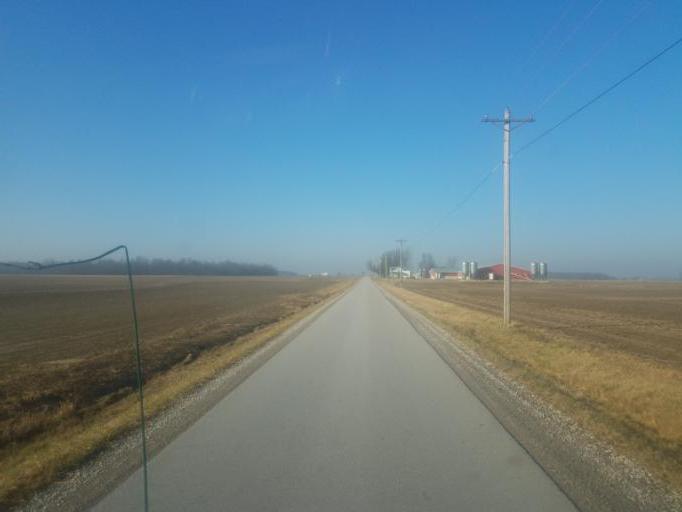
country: US
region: Ohio
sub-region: Huron County
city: Willard
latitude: 41.0083
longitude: -82.9179
